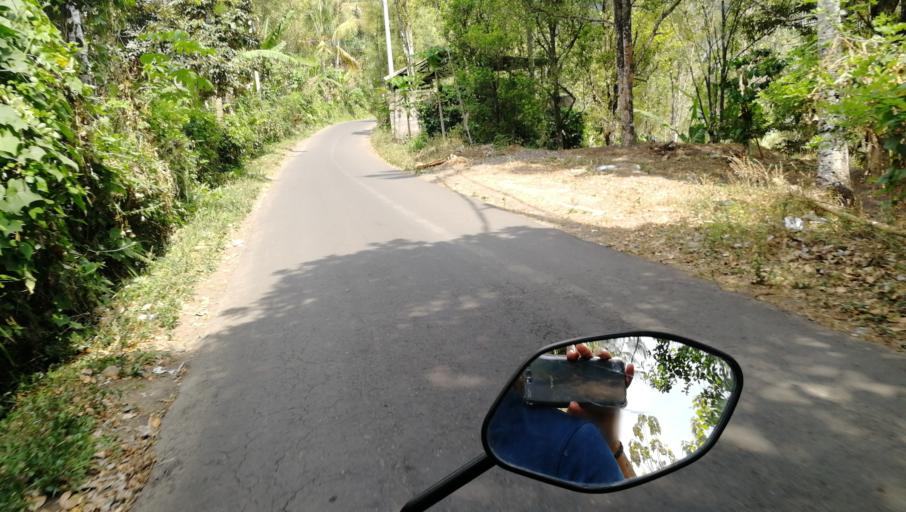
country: ID
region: Bali
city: Munduk
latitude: -8.2688
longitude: 115.0475
